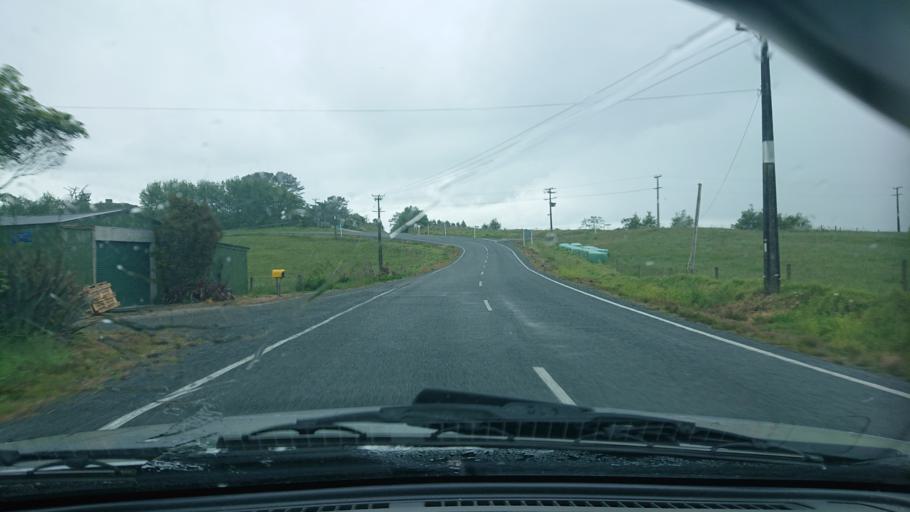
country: NZ
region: Auckland
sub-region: Auckland
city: Wellsford
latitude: -36.3293
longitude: 174.4144
